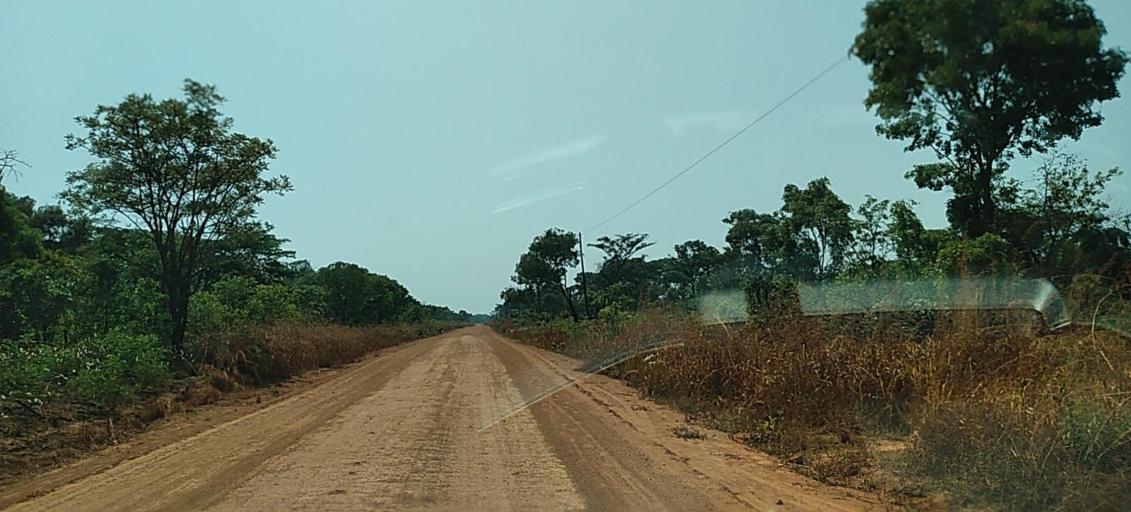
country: ZM
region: North-Western
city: Kansanshi
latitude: -11.9935
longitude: 26.6347
